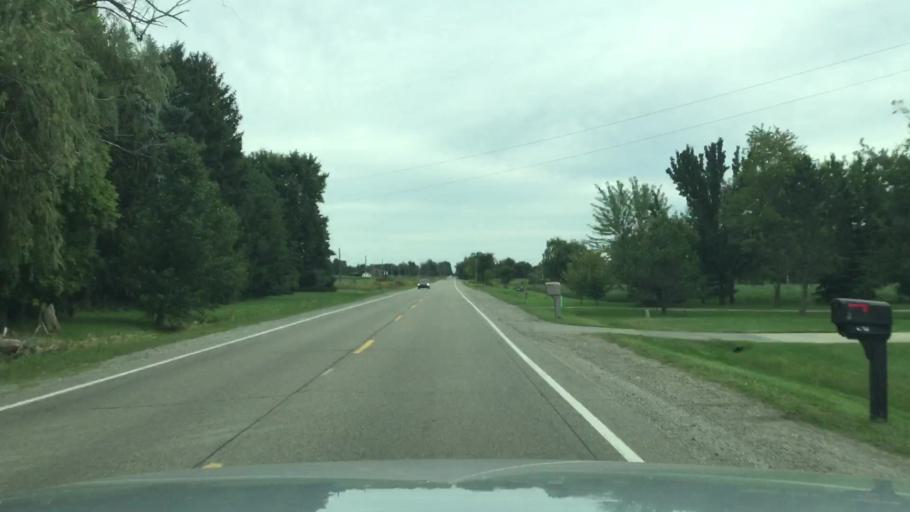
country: US
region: Michigan
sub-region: Genesee County
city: Swartz Creek
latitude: 42.9570
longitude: -83.8851
